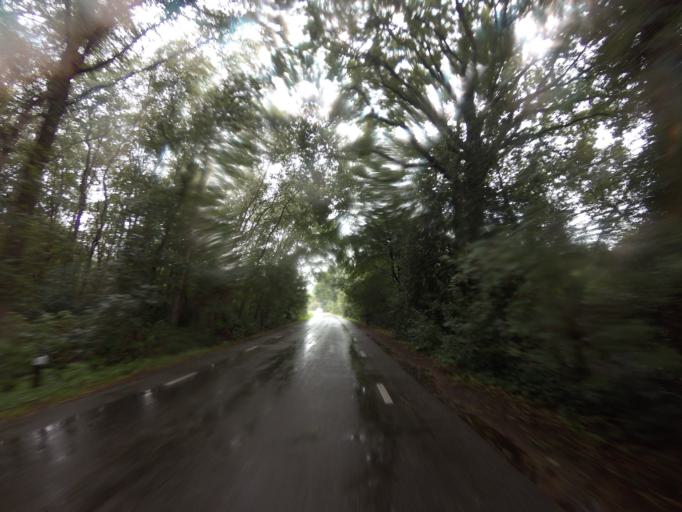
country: NL
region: Drenthe
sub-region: Gemeente Hoogeveen
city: Hoogeveen
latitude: 52.6420
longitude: 6.4444
